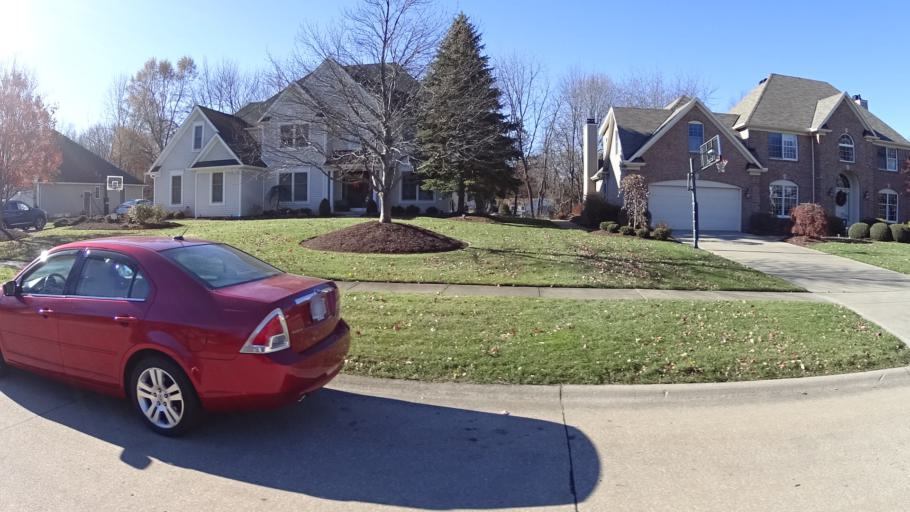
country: US
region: Ohio
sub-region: Lorain County
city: Avon Center
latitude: 41.4591
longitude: -82.0288
